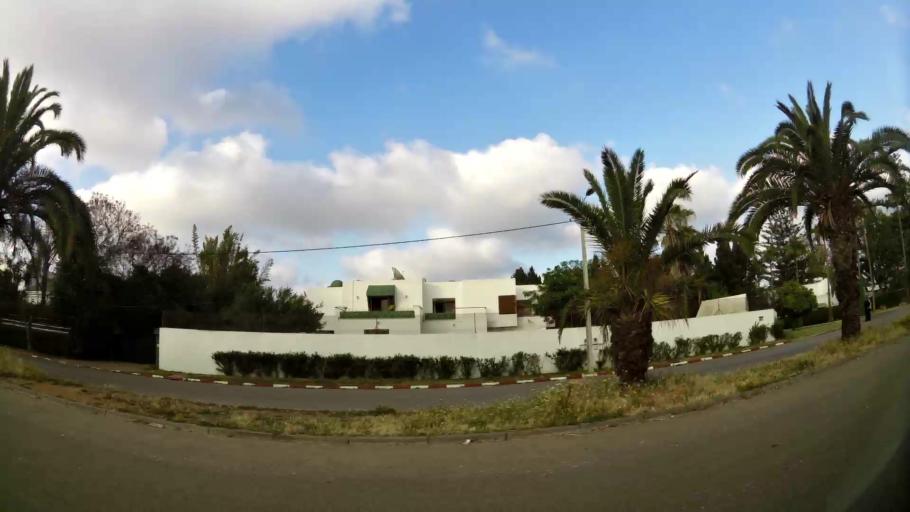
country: MA
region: Rabat-Sale-Zemmour-Zaer
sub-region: Rabat
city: Rabat
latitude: 33.9659
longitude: -6.8464
